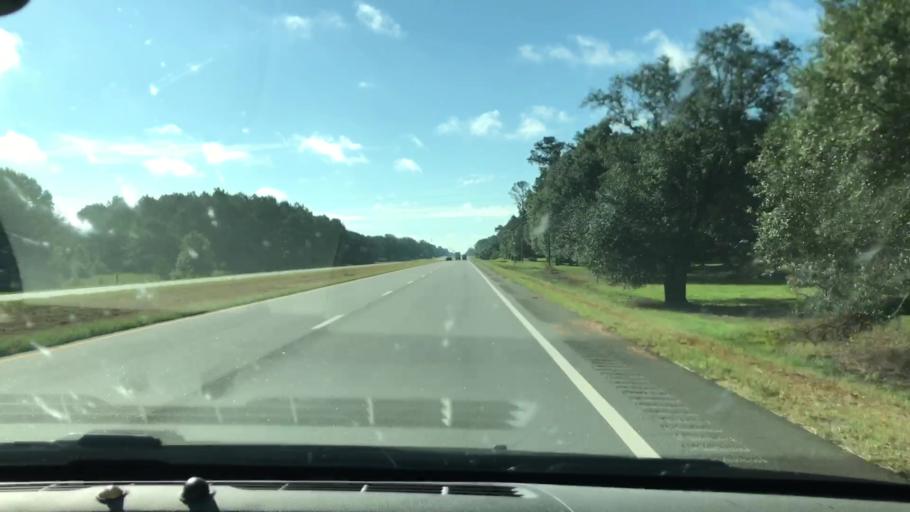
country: US
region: Georgia
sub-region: Lee County
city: Leesburg
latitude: 31.6764
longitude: -84.2952
